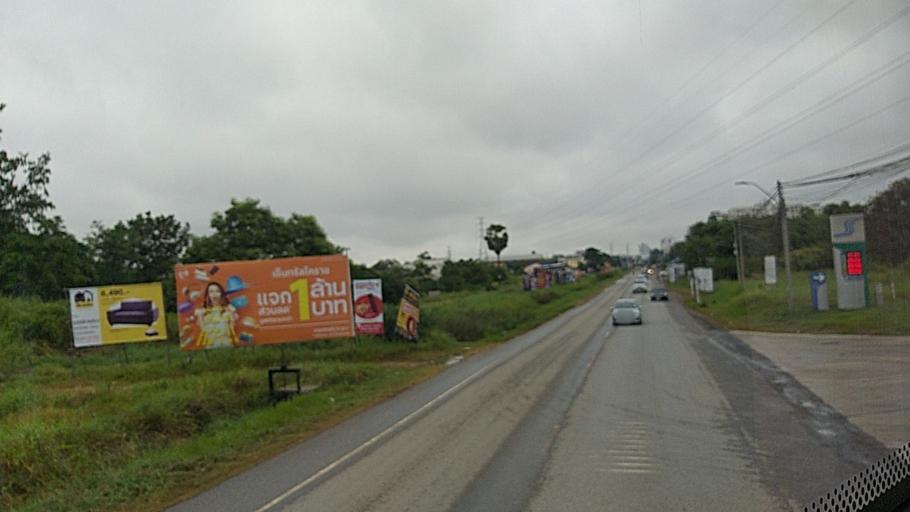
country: TH
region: Nakhon Ratchasima
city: Nakhon Ratchasima
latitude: 14.9951
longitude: 102.0918
